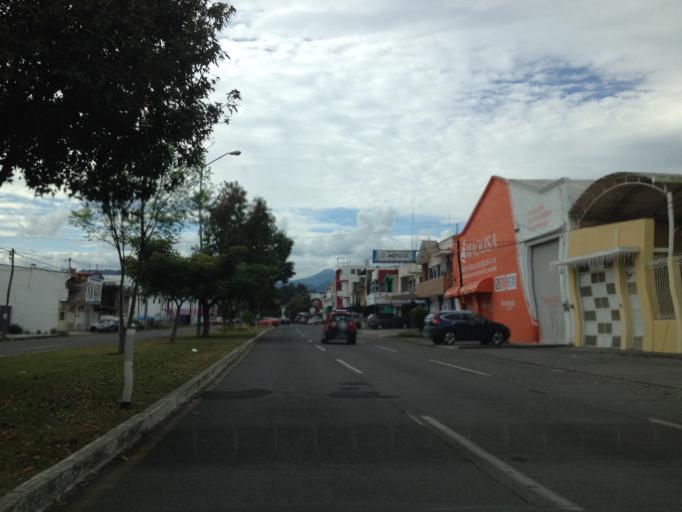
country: MX
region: Michoacan
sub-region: Uruapan
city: Uruapan
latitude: 19.4042
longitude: -102.0469
